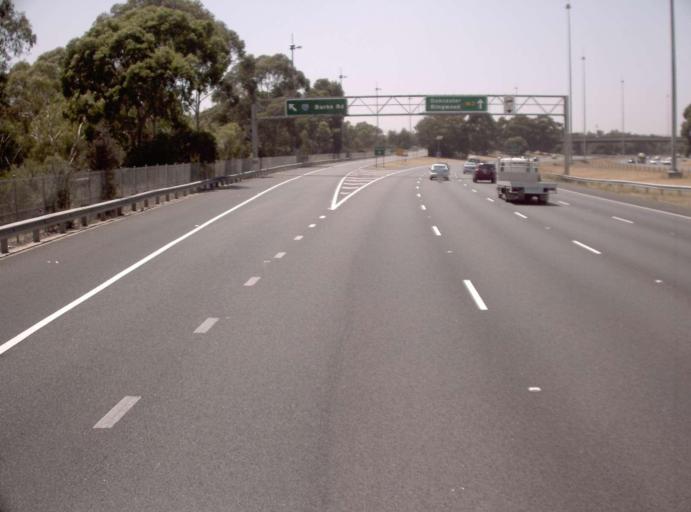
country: AU
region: Victoria
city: Ivanhoe East
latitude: -37.7863
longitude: 145.0578
